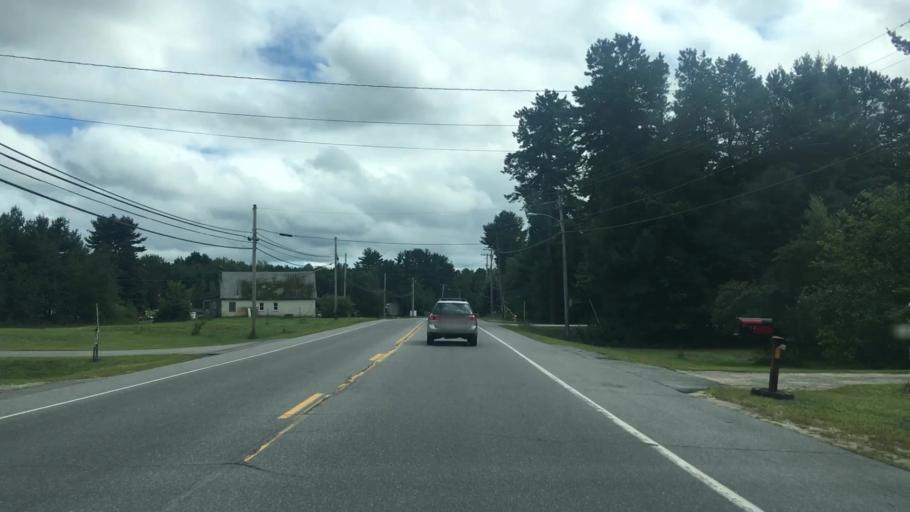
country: US
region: Maine
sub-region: York County
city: Waterboro
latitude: 43.5454
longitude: -70.7103
